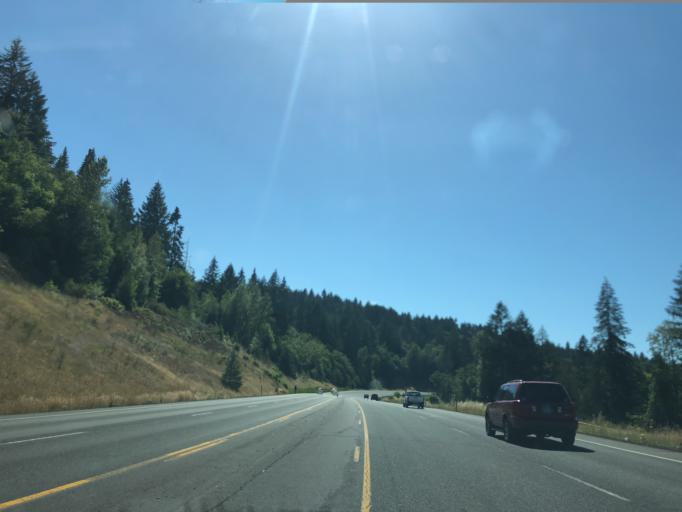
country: US
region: Oregon
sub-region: Linn County
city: Sweet Home
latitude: 44.4049
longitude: -122.7538
